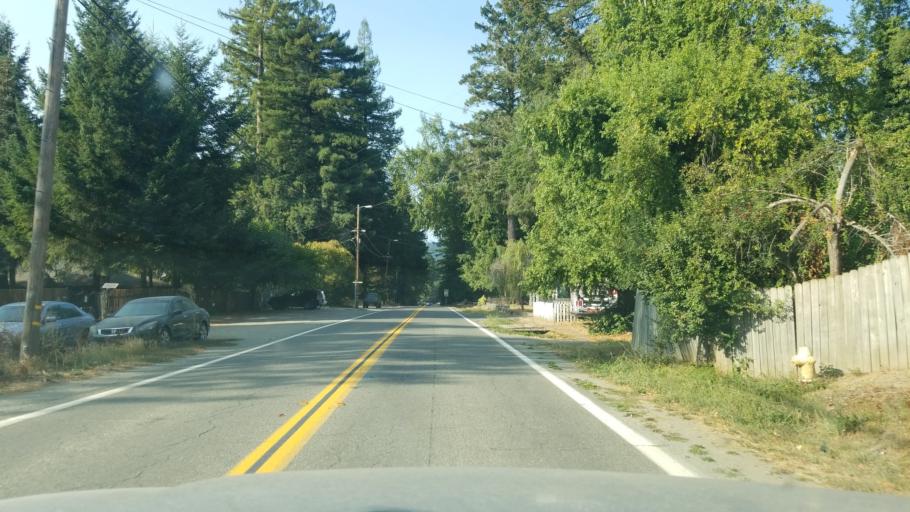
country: US
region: California
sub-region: Humboldt County
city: Redway
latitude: 40.2317
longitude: -123.8244
